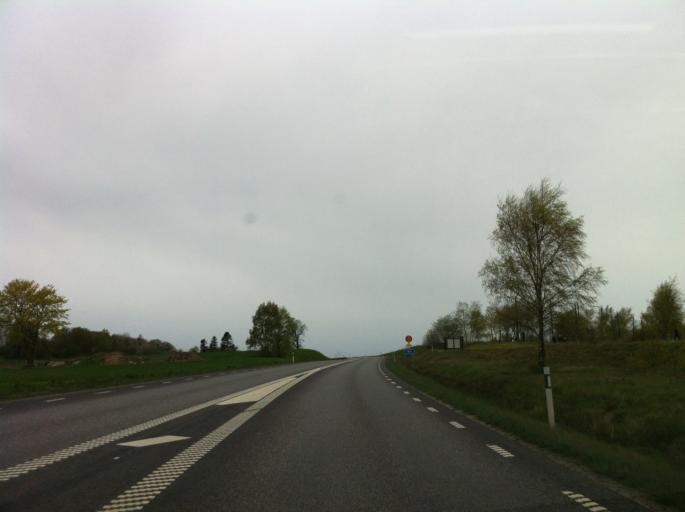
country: SE
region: Halland
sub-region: Falkenbergs Kommun
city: Falkenberg
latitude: 56.9591
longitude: 12.5542
